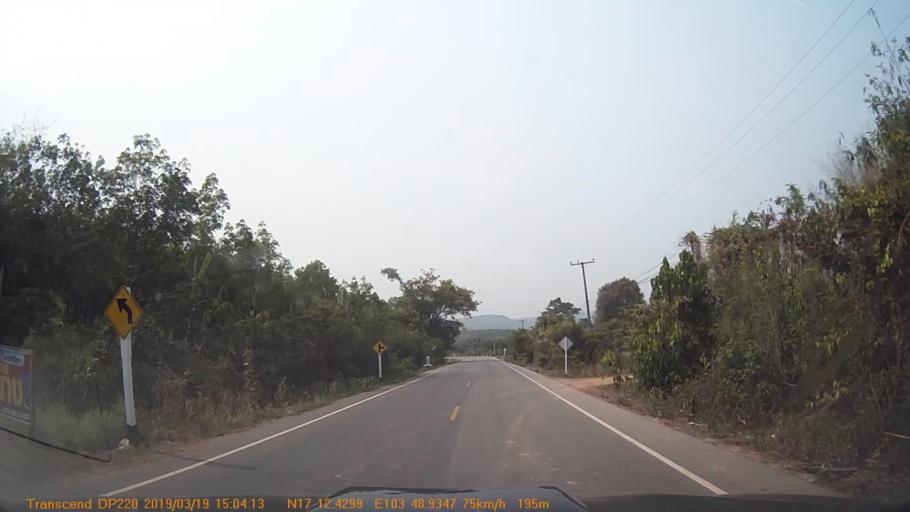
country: TH
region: Sakon Nakhon
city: Nikhom Nam Un
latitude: 17.2074
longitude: 103.8155
